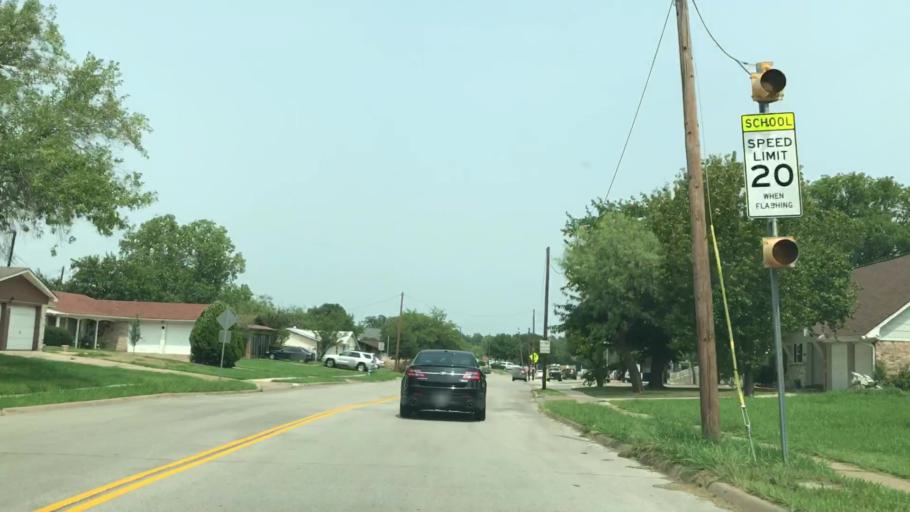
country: US
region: Texas
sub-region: Dallas County
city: Irving
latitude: 32.8428
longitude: -97.0049
